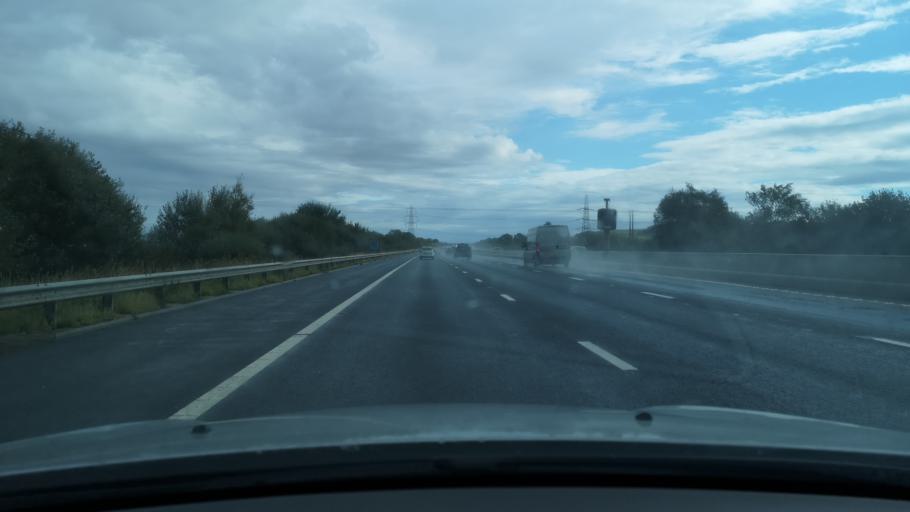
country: GB
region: England
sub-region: City and Borough of Wakefield
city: Knottingley
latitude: 53.6948
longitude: -1.2116
